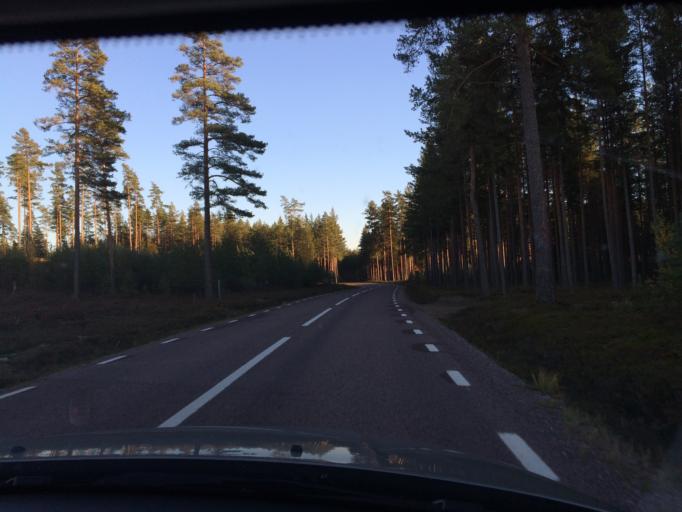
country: SE
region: Gaevleborg
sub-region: Sandvikens Kommun
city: Arsunda
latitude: 60.4186
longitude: 16.7021
